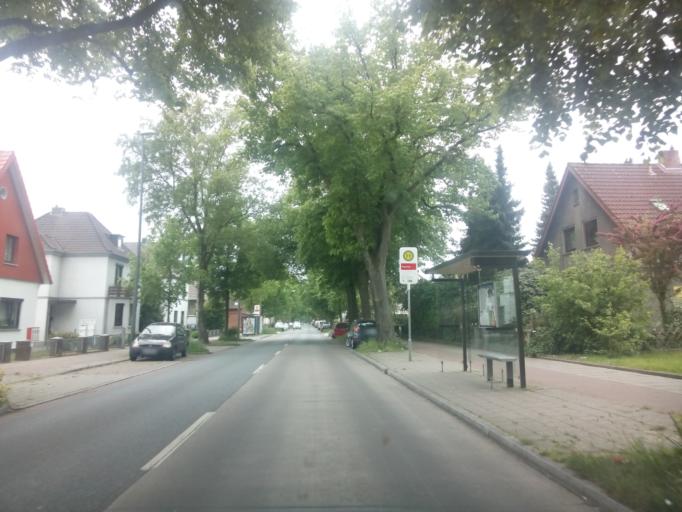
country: DE
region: Lower Saxony
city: Schwanewede
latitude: 53.2049
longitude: 8.5770
